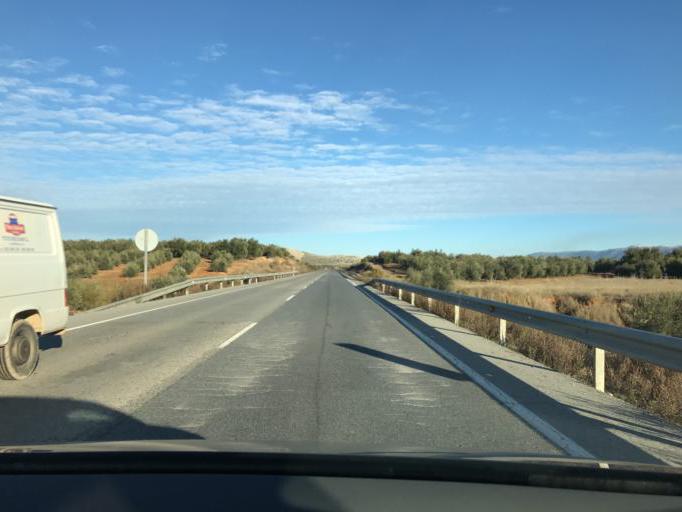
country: ES
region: Andalusia
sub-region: Provincia de Granada
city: Iznalloz
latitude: 37.4005
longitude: -3.5451
